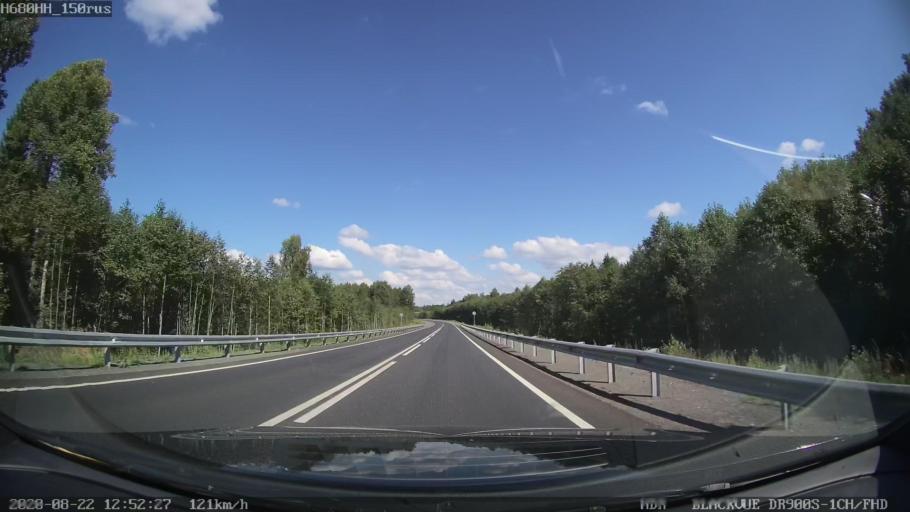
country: RU
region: Tverskaya
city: Rameshki
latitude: 57.5021
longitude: 36.2620
